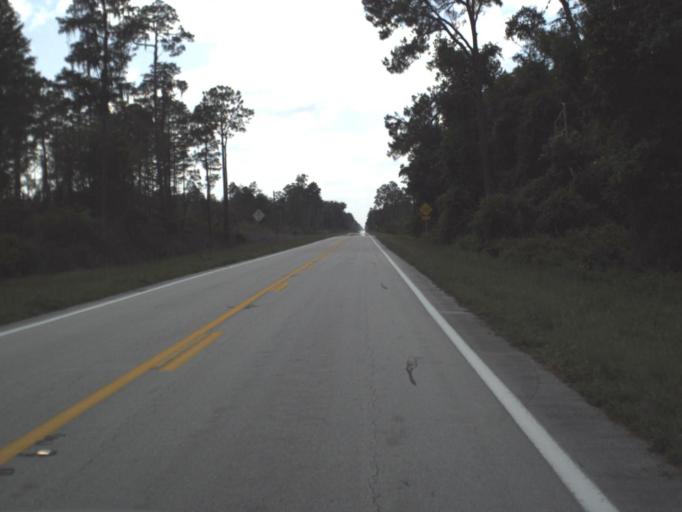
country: US
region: Florida
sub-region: Baker County
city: Macclenny
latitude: 30.5186
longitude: -82.2821
